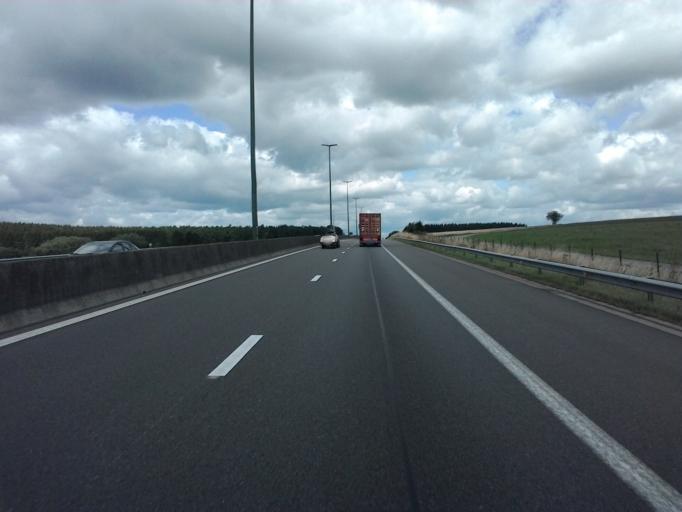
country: BE
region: Wallonia
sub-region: Province du Luxembourg
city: Leglise
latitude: 49.7789
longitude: 5.5410
